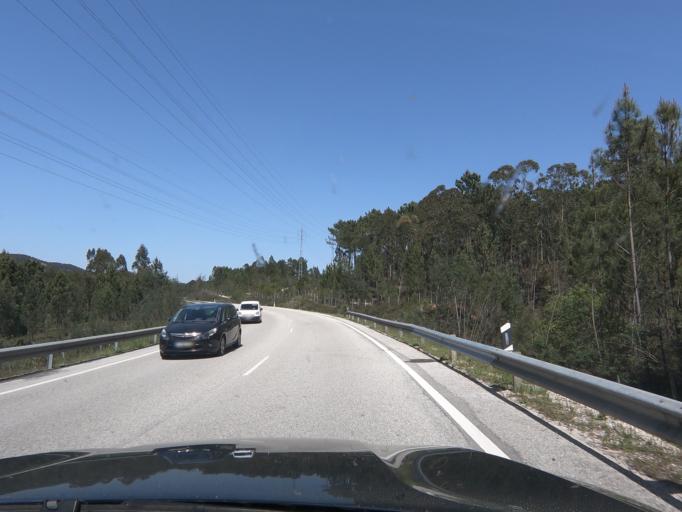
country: PT
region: Coimbra
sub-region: Miranda do Corvo
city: Miranda do Corvo
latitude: 40.0971
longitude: -8.3120
